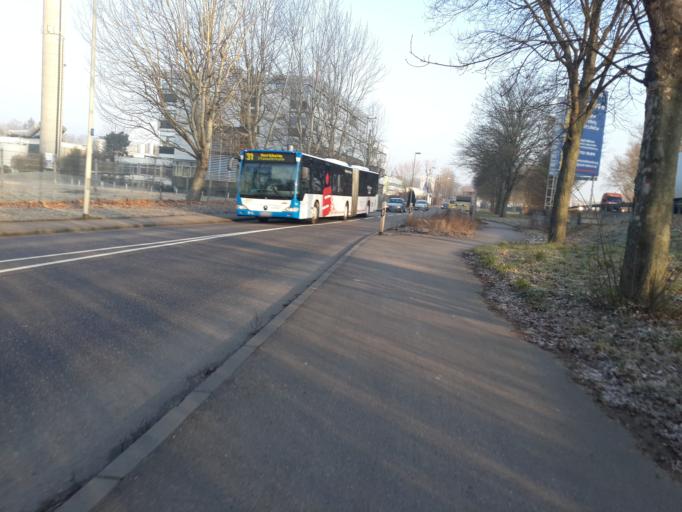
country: DE
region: Baden-Wuerttemberg
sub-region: Regierungsbezirk Stuttgart
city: Neckarsulm
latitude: 49.1787
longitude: 9.2015
